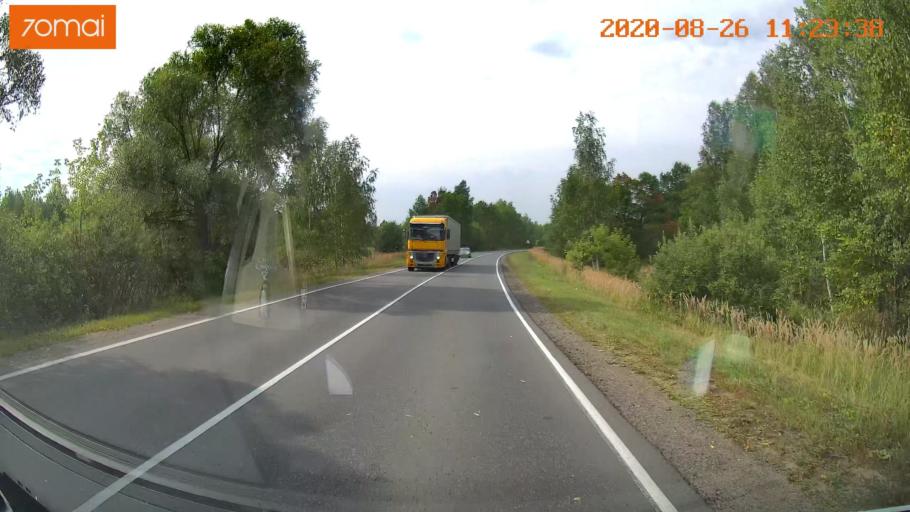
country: RU
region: Rjazan
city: Shilovo
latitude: 54.3503
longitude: 41.0067
